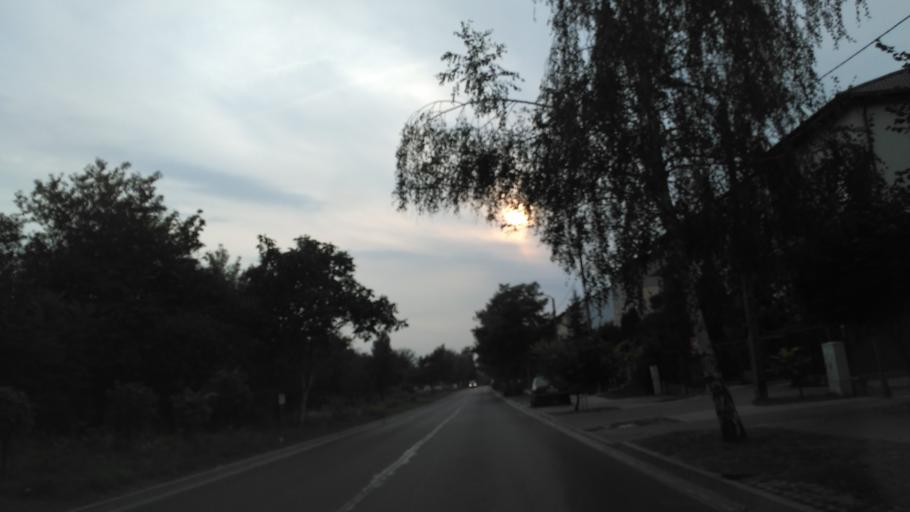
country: PL
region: Lublin Voivodeship
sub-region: Powiat lubelski
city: Lublin
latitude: 51.2252
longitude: 22.5924
